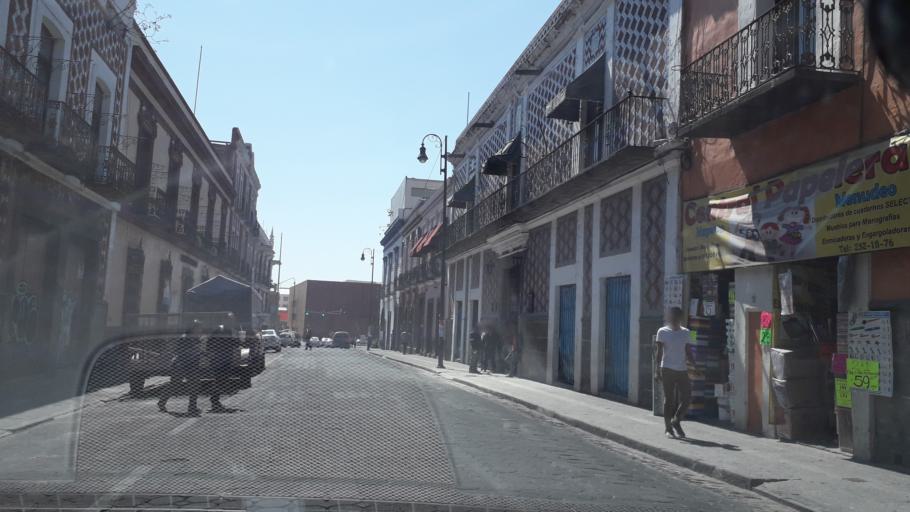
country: MX
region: Puebla
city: Puebla
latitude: 19.0455
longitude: -98.1930
